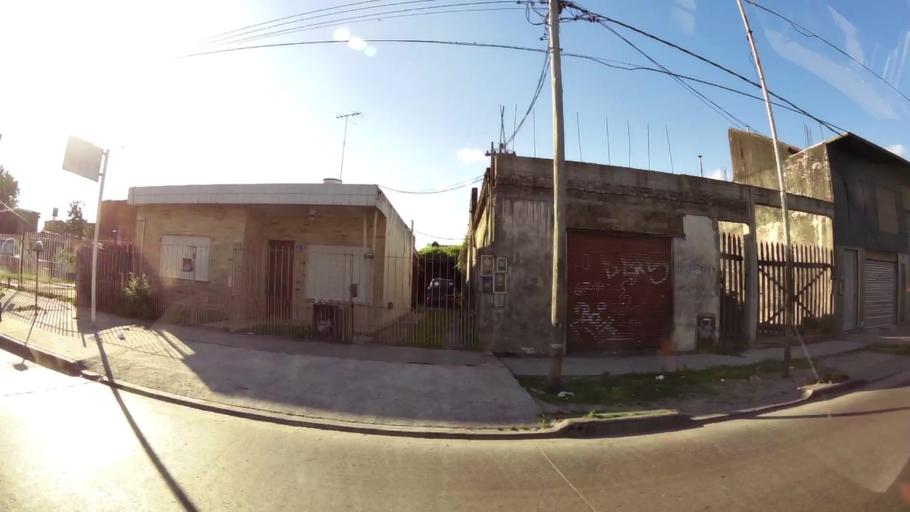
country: AR
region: Buenos Aires
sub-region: Partido de Moron
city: Moron
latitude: -34.6847
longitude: -58.6209
